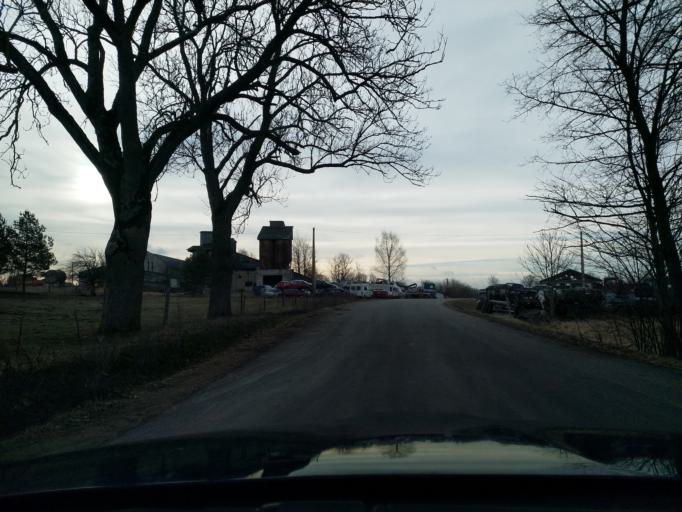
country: LV
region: Kuldigas Rajons
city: Kuldiga
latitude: 56.9602
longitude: 22.0090
